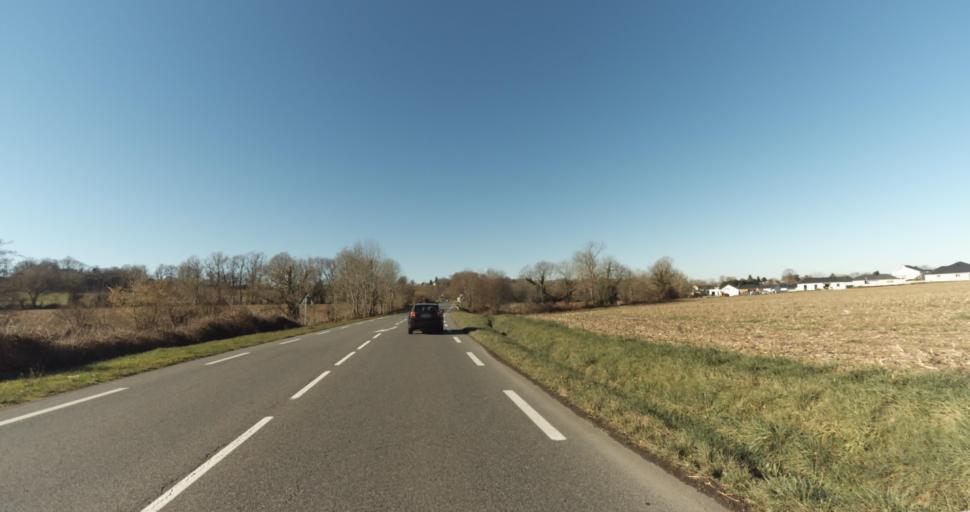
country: FR
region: Aquitaine
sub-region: Departement des Pyrenees-Atlantiques
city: Morlaas
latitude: 43.3377
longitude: -0.2558
